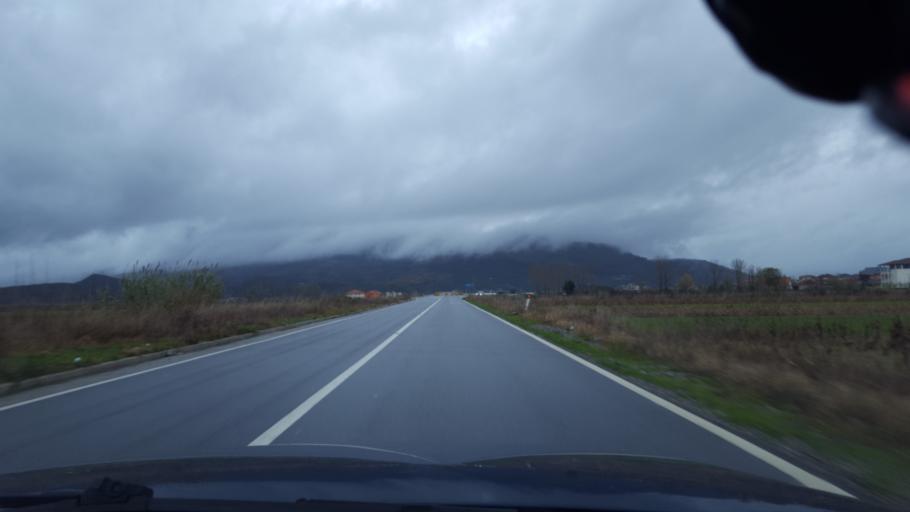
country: AL
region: Shkoder
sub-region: Rrethi i Shkodres
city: Berdica e Madhe
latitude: 42.0039
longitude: 19.4803
